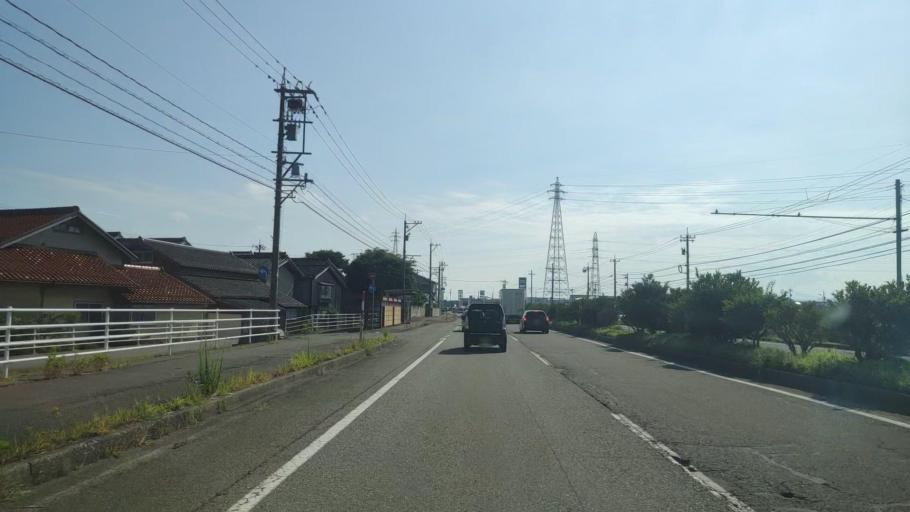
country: JP
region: Ishikawa
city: Matsuto
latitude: 36.4981
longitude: 136.5390
